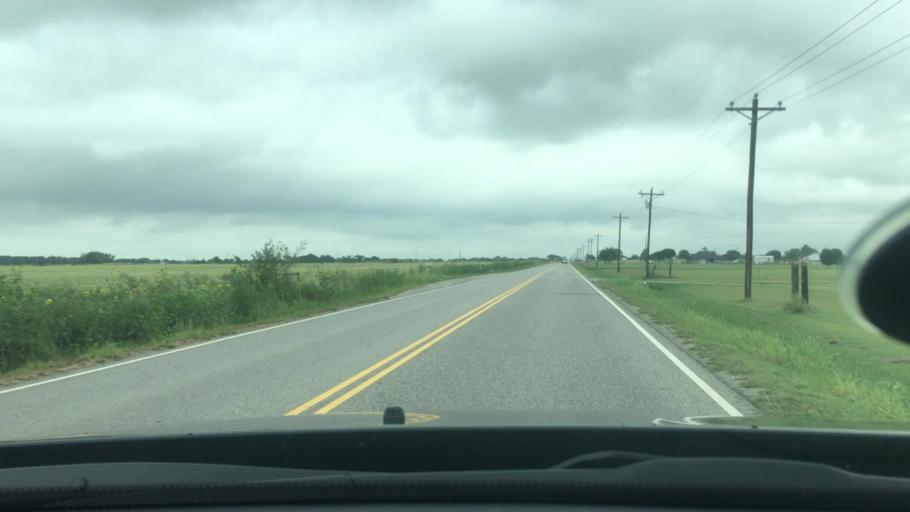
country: US
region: Oklahoma
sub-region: Bryan County
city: Colbert
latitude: 33.9048
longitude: -96.5006
